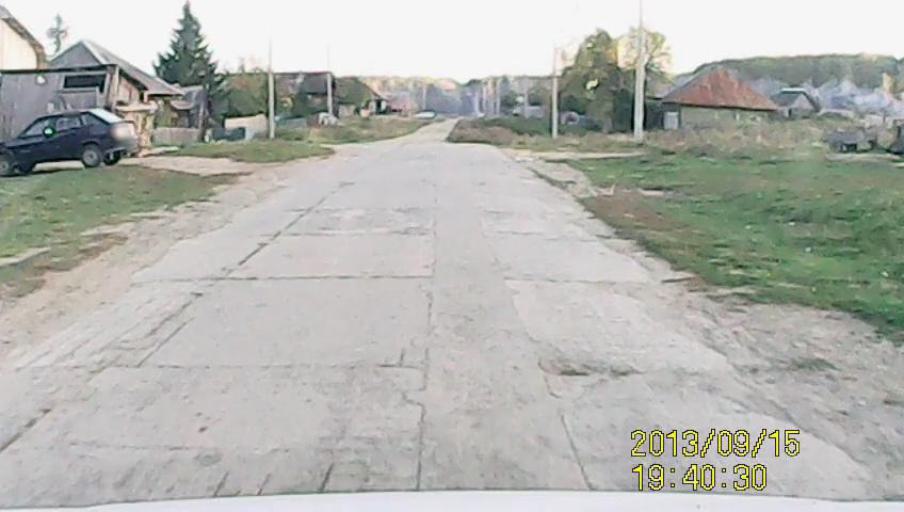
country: RU
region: Chelyabinsk
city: Kyshtym
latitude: 55.8480
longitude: 60.4815
